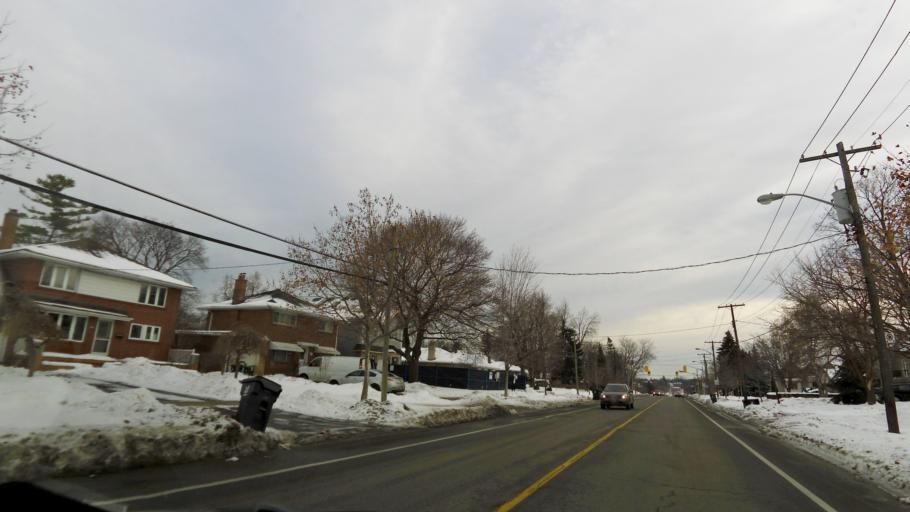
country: CA
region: Ontario
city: Etobicoke
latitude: 43.6652
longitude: -79.5590
